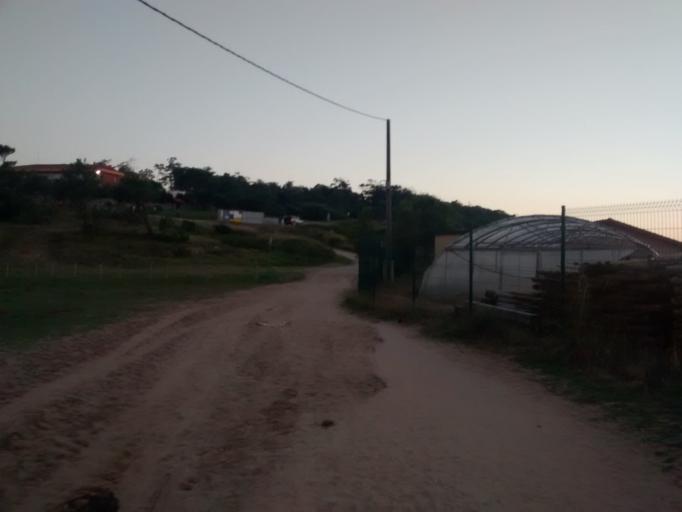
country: ES
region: Cantabria
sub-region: Provincia de Cantabria
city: Santander
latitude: 43.4602
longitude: -3.7264
